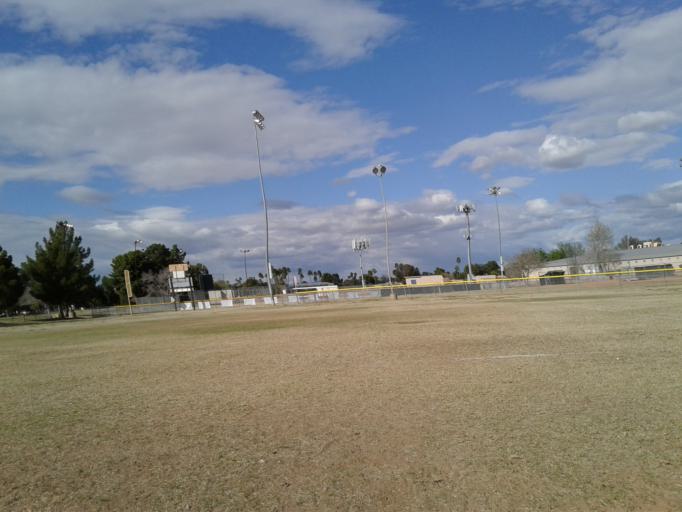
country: US
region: Arizona
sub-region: Maricopa County
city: Paradise Valley
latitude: 33.6047
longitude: -111.9556
